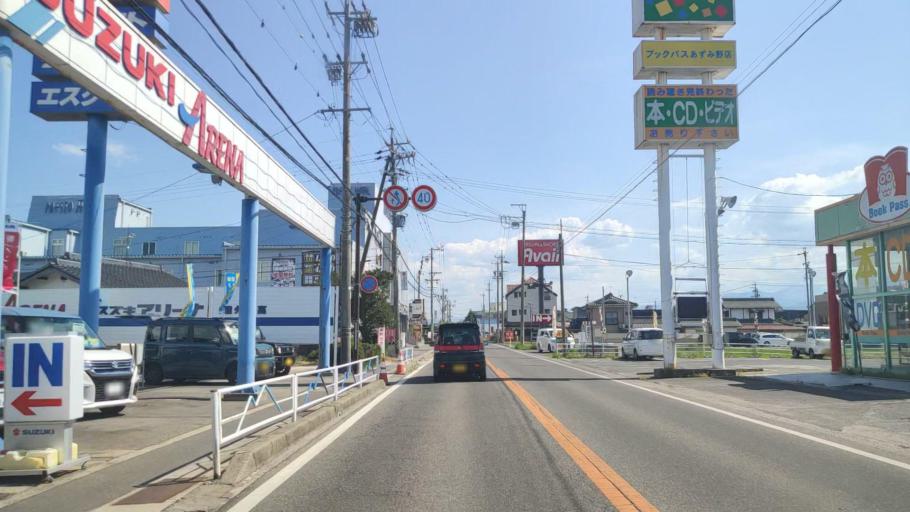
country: JP
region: Nagano
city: Hotaka
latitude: 36.3228
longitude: 137.8935
